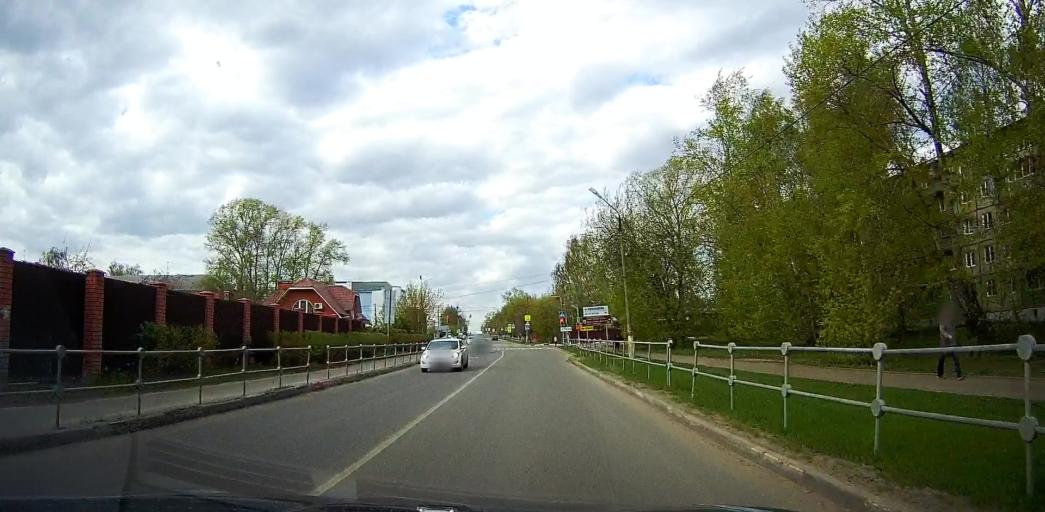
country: RU
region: Moskovskaya
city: Pavlovskiy Posad
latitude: 55.7687
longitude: 38.6555
